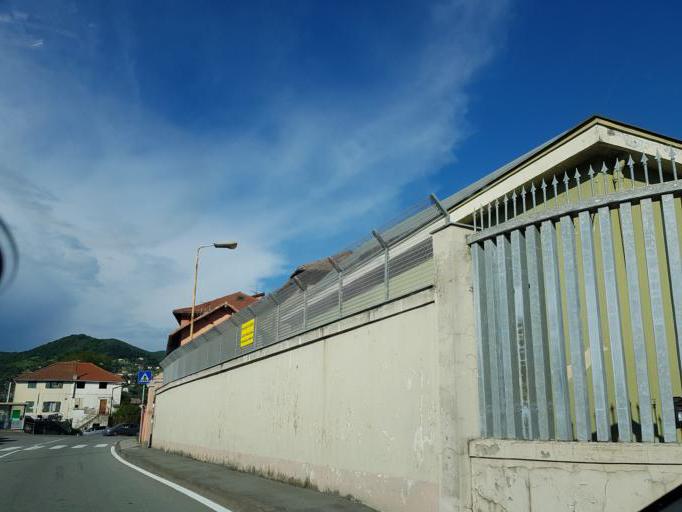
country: IT
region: Liguria
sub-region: Provincia di Genova
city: Manesseno
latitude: 44.4740
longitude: 8.9129
